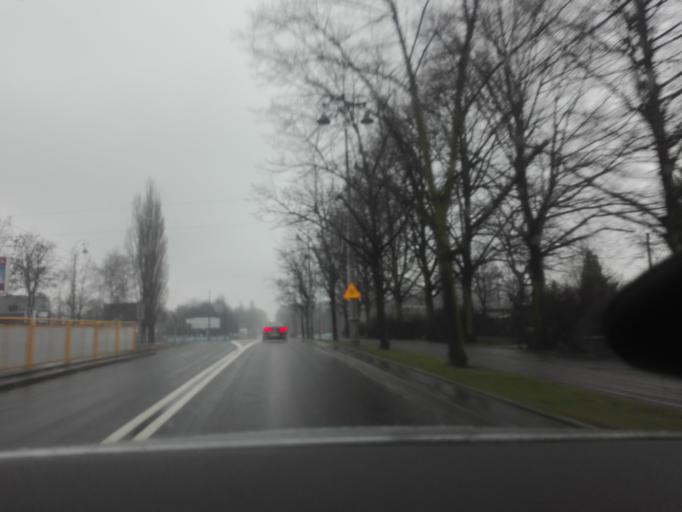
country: PL
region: Silesian Voivodeship
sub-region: Katowice
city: Katowice
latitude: 50.2484
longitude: 19.0120
